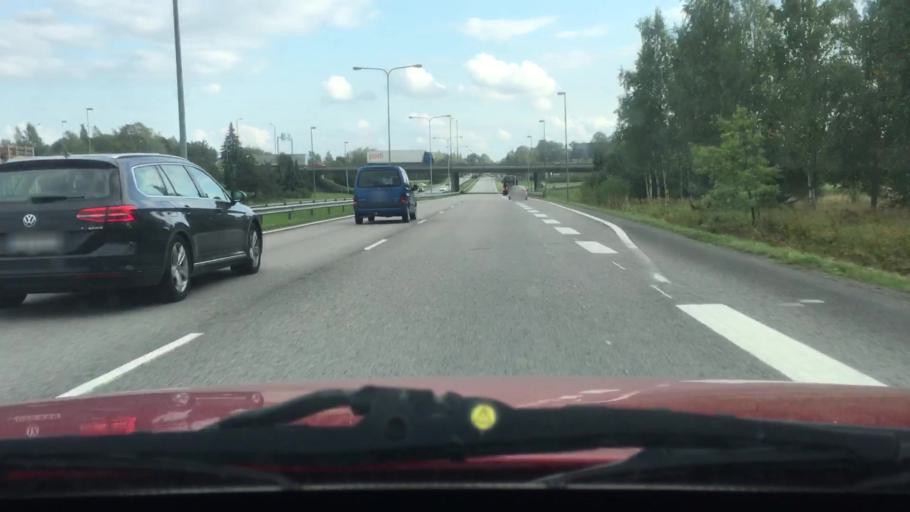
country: FI
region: Varsinais-Suomi
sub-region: Turku
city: Raisio
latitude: 60.4897
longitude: 22.1726
